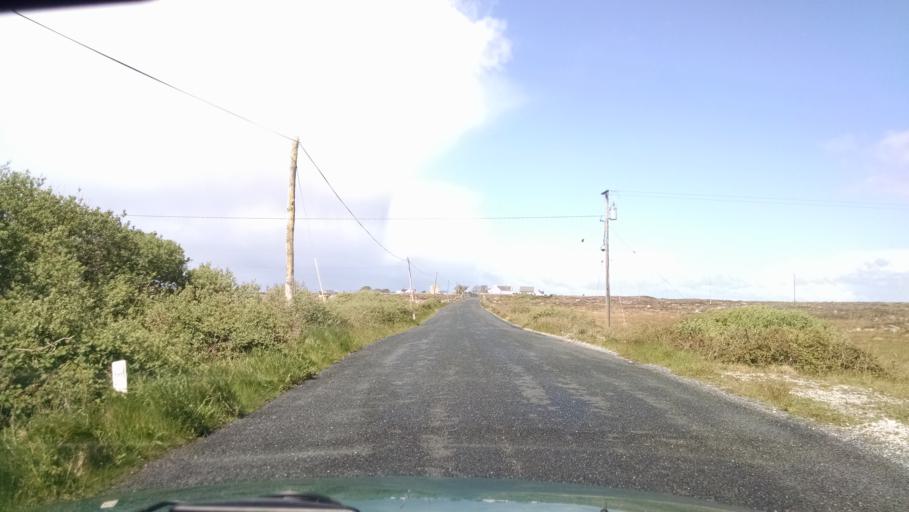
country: IE
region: Connaught
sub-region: County Galway
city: Oughterard
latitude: 53.2425
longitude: -9.5115
